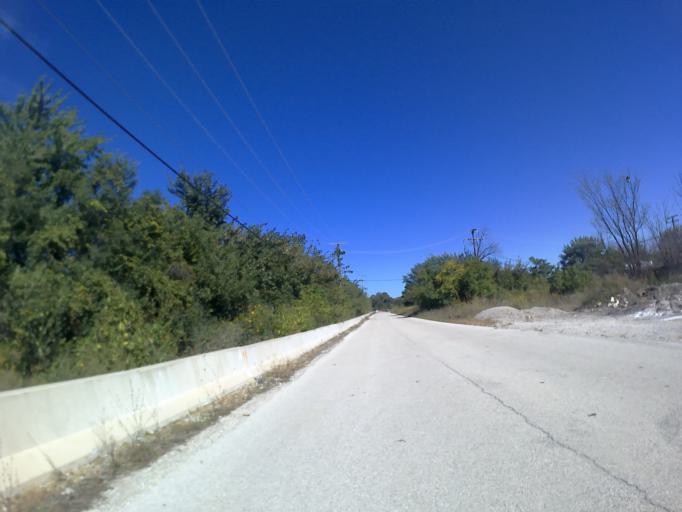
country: US
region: Illinois
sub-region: Cook County
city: Lemont
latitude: 41.6860
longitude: -87.9872
